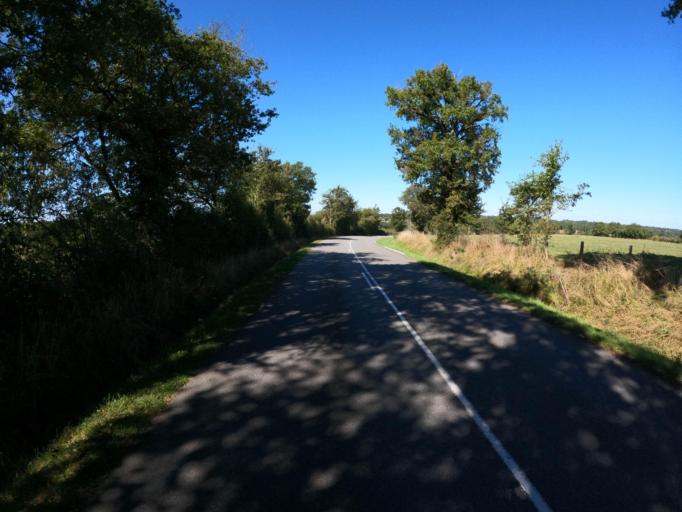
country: FR
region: Limousin
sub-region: Departement de la Haute-Vienne
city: Le Dorat
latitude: 46.2274
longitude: 1.0633
